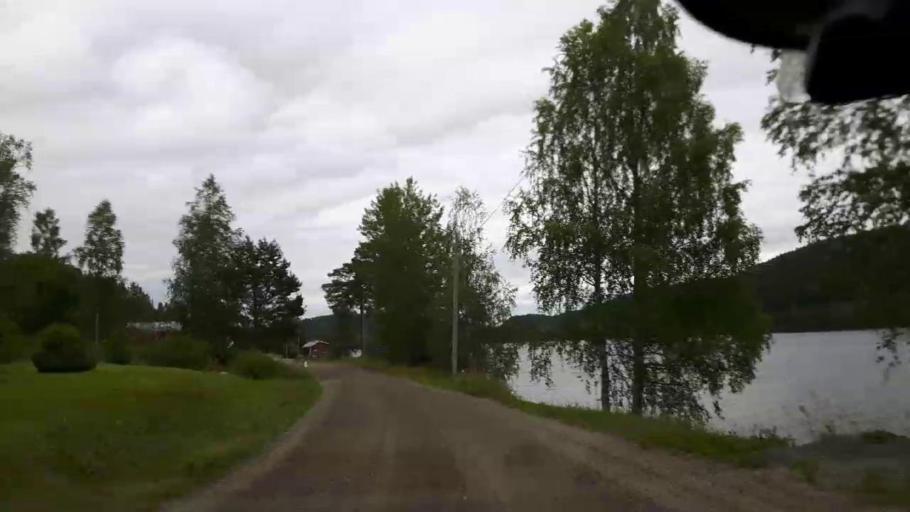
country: SE
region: Jaemtland
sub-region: Braecke Kommun
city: Braecke
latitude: 63.0028
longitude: 15.3812
